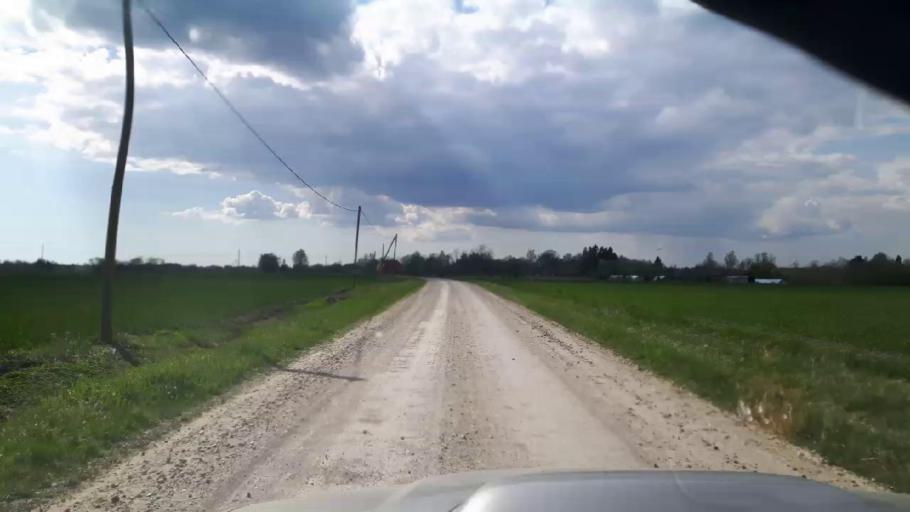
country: EE
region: Paernumaa
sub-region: Sindi linn
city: Sindi
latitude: 58.4195
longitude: 24.7194
